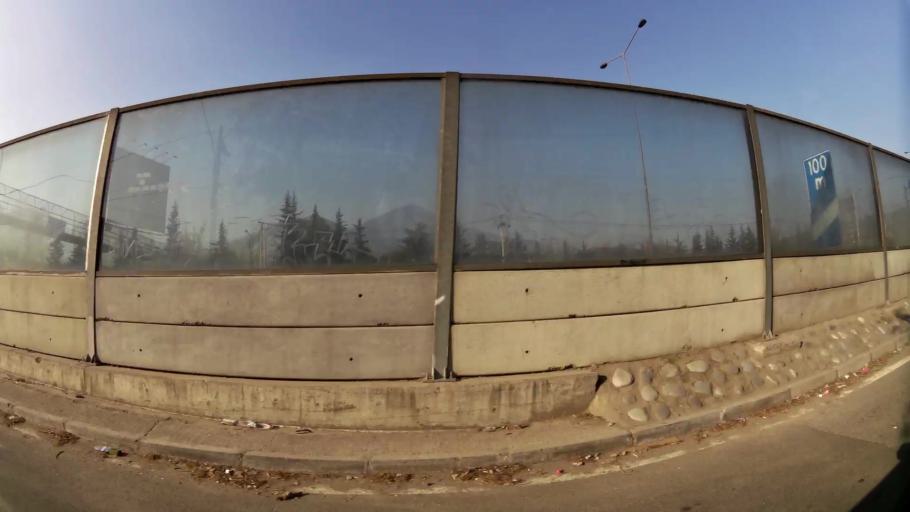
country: CL
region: Santiago Metropolitan
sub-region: Provincia de Santiago
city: Santiago
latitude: -33.3898
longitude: -70.6319
